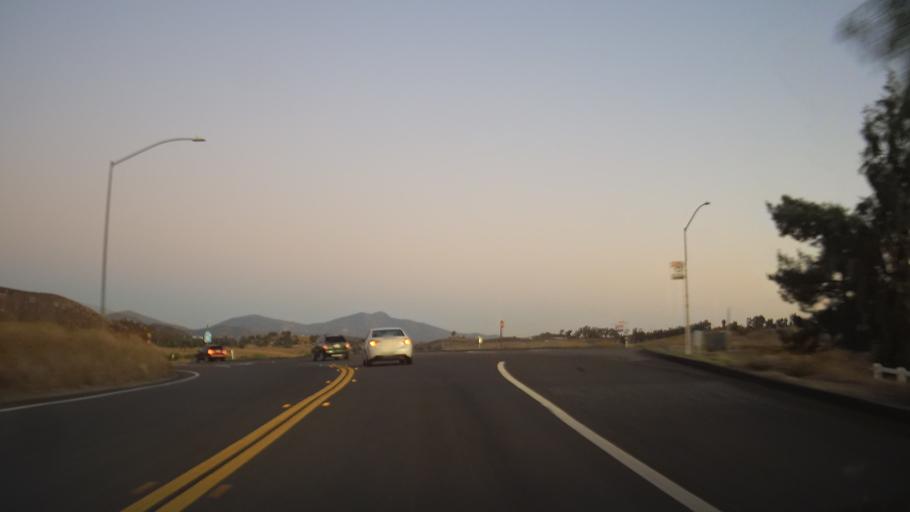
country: US
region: California
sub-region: San Diego County
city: San Diego Country Estates
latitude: 33.0796
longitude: -116.7829
